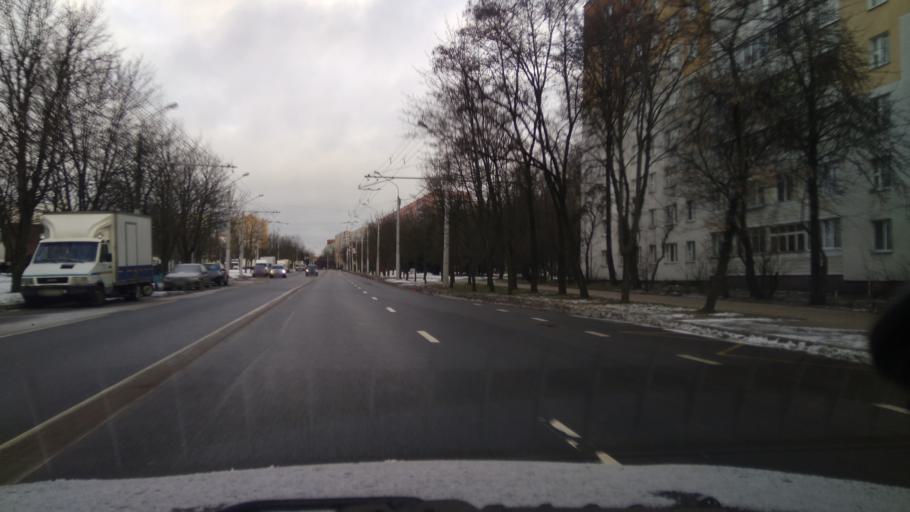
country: BY
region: Minsk
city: Novoye Medvezhino
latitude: 53.8983
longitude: 27.4815
